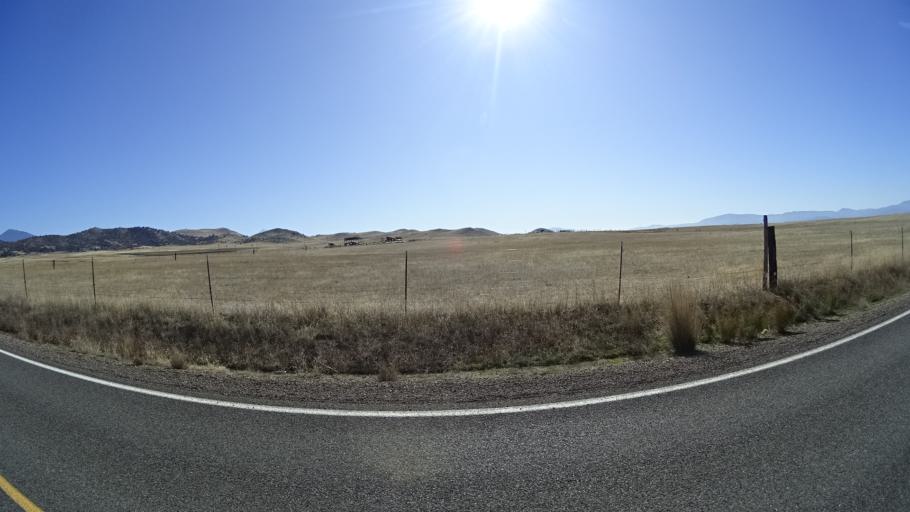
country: US
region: California
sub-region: Siskiyou County
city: Montague
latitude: 41.8082
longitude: -122.4182
